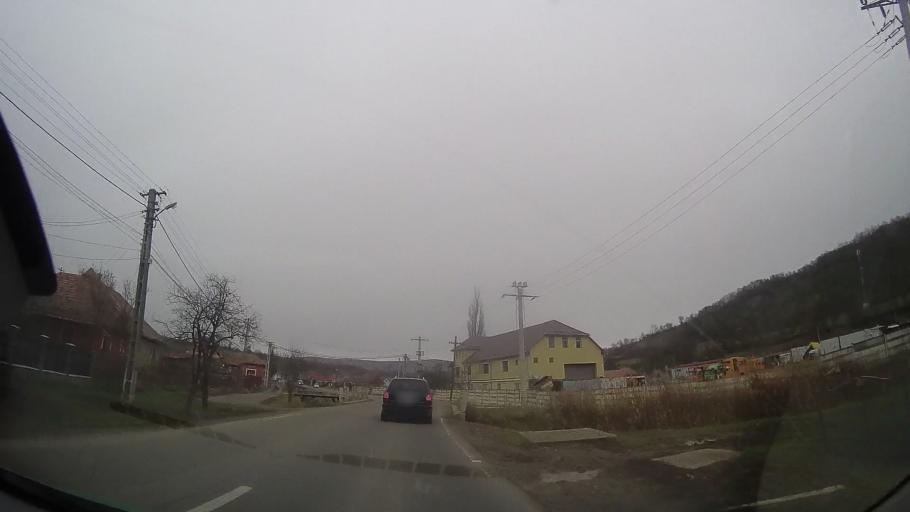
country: RO
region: Mures
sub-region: Comuna Ceausu de Campie
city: Ceausu de Campie
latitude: 46.6372
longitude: 24.5168
